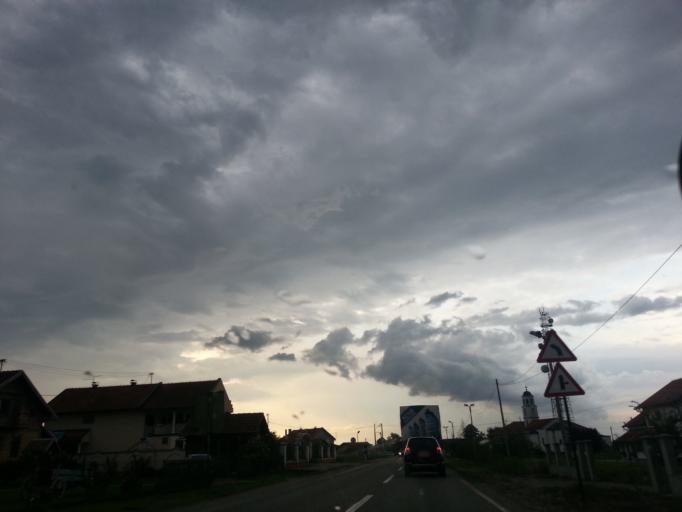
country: BA
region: Republika Srpska
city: Velika Obarska
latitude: 44.8085
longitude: 19.0681
